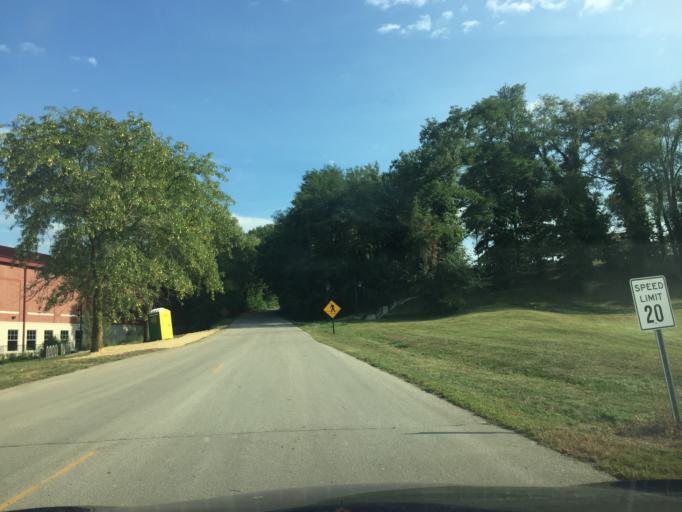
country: US
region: Kansas
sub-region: Leavenworth County
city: Leavenworth
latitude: 39.3582
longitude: -94.9221
